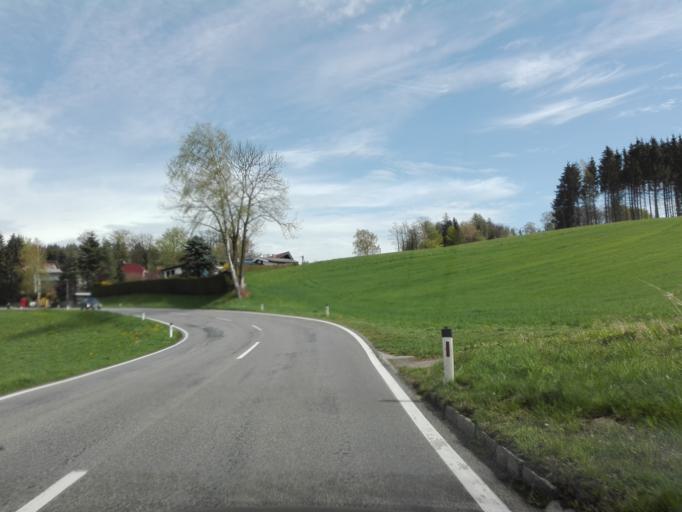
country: AT
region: Upper Austria
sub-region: Politischer Bezirk Urfahr-Umgebung
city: Eidenberg
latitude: 48.3520
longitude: 14.2388
